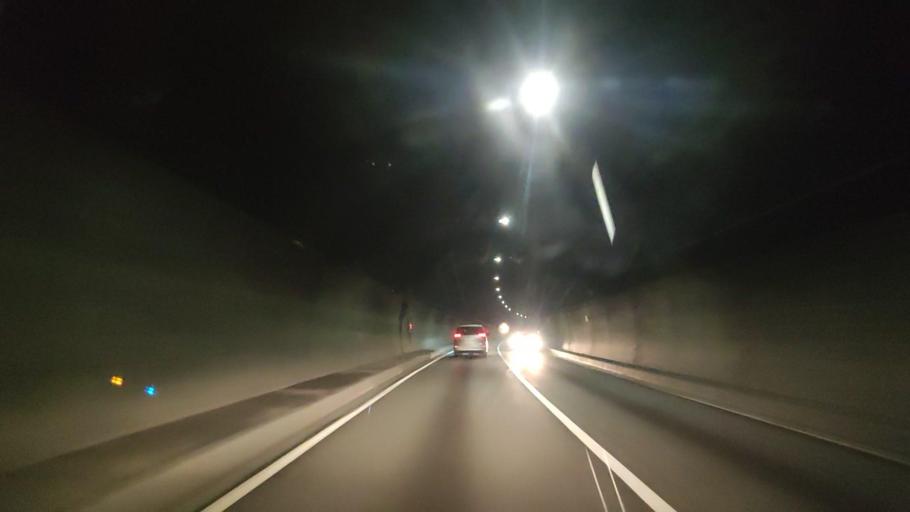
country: JP
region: Nagano
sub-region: Kitaazumi Gun
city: Hakuba
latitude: 36.8075
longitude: 137.9130
